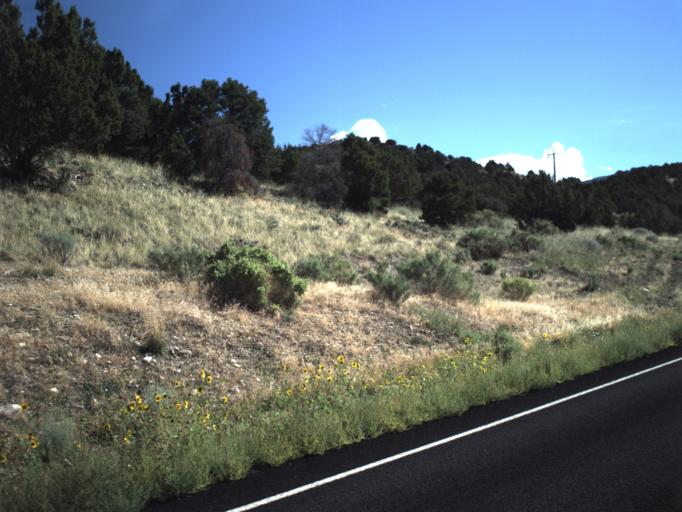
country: US
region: Utah
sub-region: Beaver County
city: Beaver
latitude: 38.2819
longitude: -112.5952
